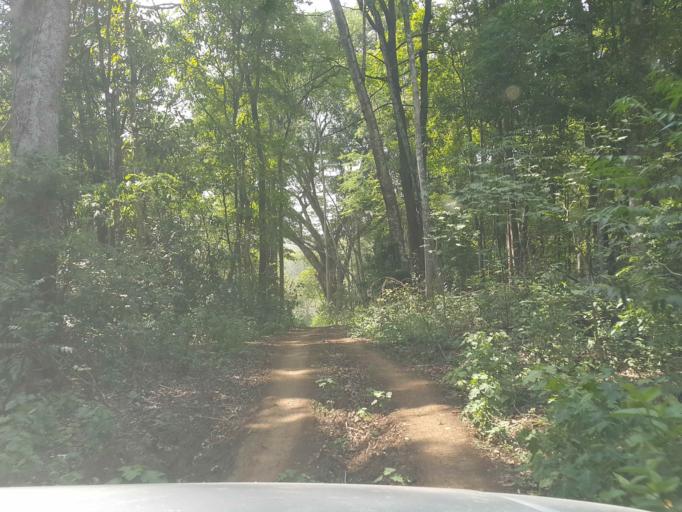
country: TH
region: Chiang Mai
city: Wiang Haeng
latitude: 19.3366
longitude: 98.7165
